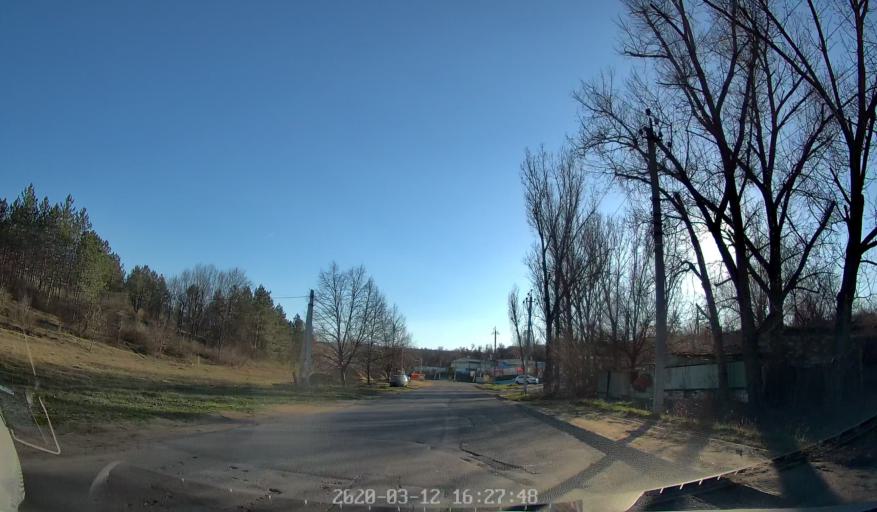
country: MD
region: Anenii Noi
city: Anenii Noi
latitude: 46.8730
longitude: 29.2279
